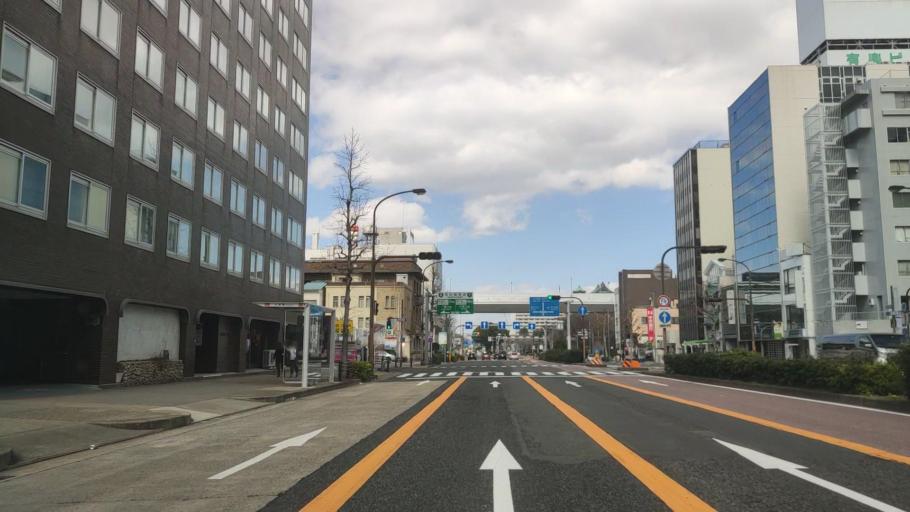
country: JP
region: Aichi
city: Nagoya-shi
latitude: 35.1765
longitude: 136.9060
